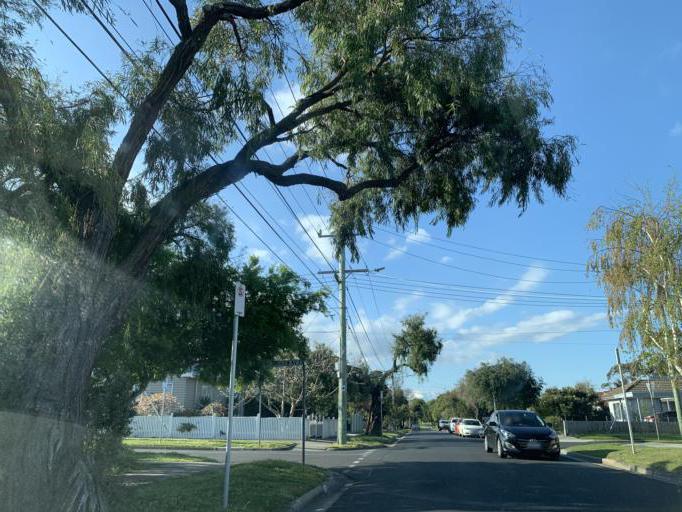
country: AU
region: Victoria
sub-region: Kingston
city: Mordialloc
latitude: -37.9945
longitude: 145.0883
